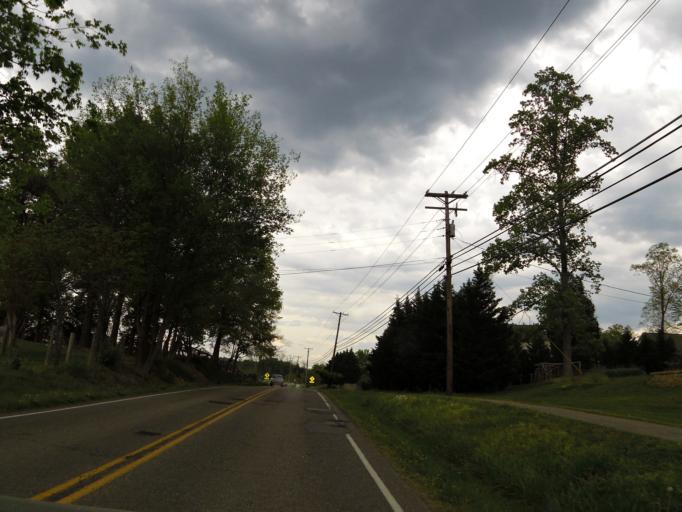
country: US
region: Tennessee
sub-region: Knox County
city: Knoxville
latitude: 35.8849
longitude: -83.8942
